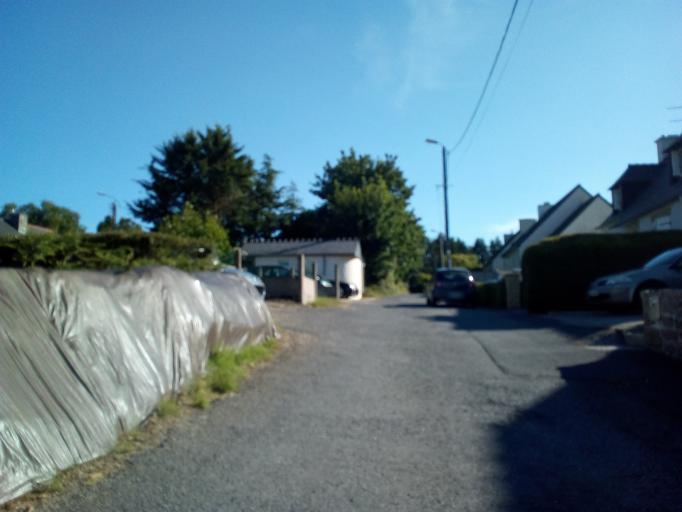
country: FR
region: Brittany
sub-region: Departement du Finistere
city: Landivisiau
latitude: 48.5055
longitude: -4.0764
